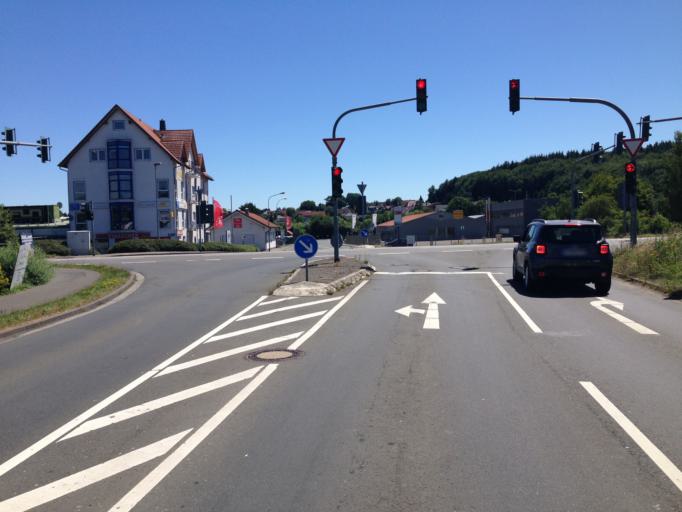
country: DE
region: Hesse
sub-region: Regierungsbezirk Giessen
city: Reiskirchen
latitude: 50.5980
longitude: 8.8224
